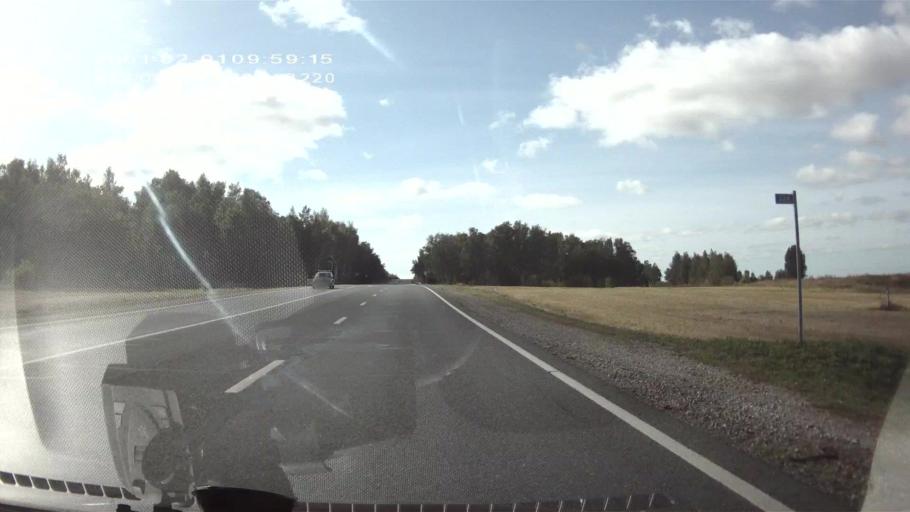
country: RU
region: Ulyanovsk
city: Krasnyy Gulyay
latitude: 54.0809
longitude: 48.2281
